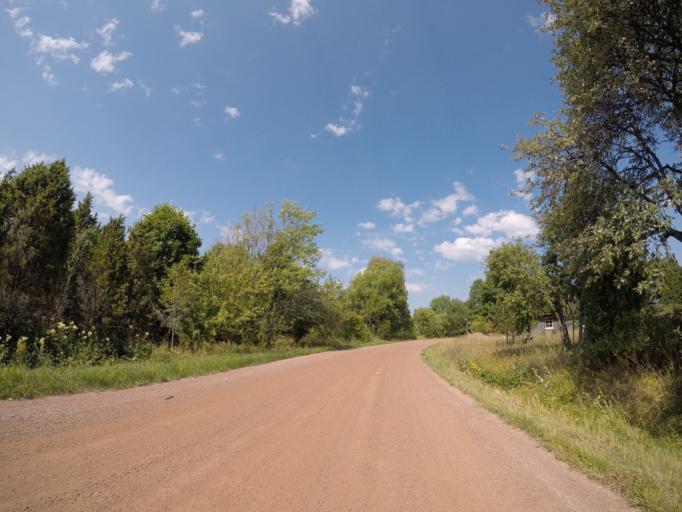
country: AX
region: Alands landsbygd
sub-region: Finstroem
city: Finstroem
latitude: 60.2140
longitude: 19.8564
